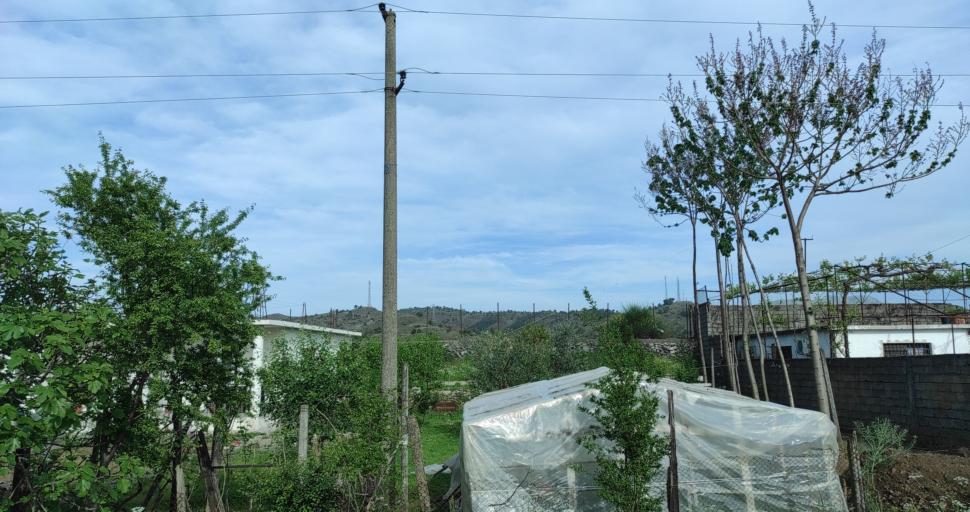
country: AL
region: Shkoder
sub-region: Rrethi i Shkodres
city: Shkoder
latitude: 42.0689
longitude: 19.5287
